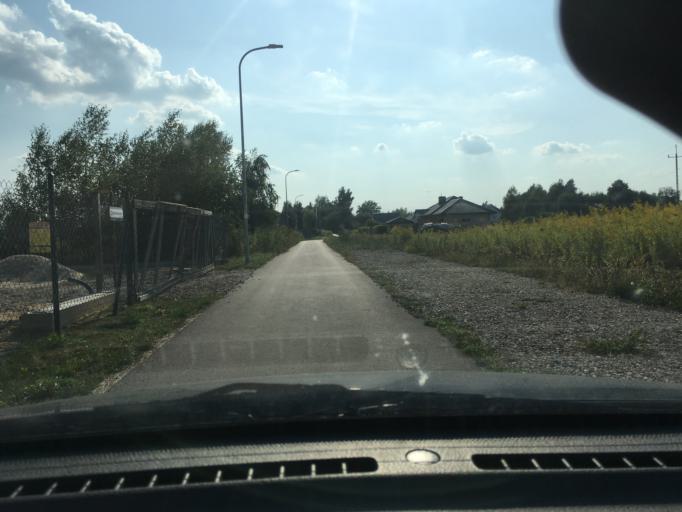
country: PL
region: Masovian Voivodeship
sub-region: Powiat piaseczynski
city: Lesznowola
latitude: 52.0525
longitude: 20.9343
